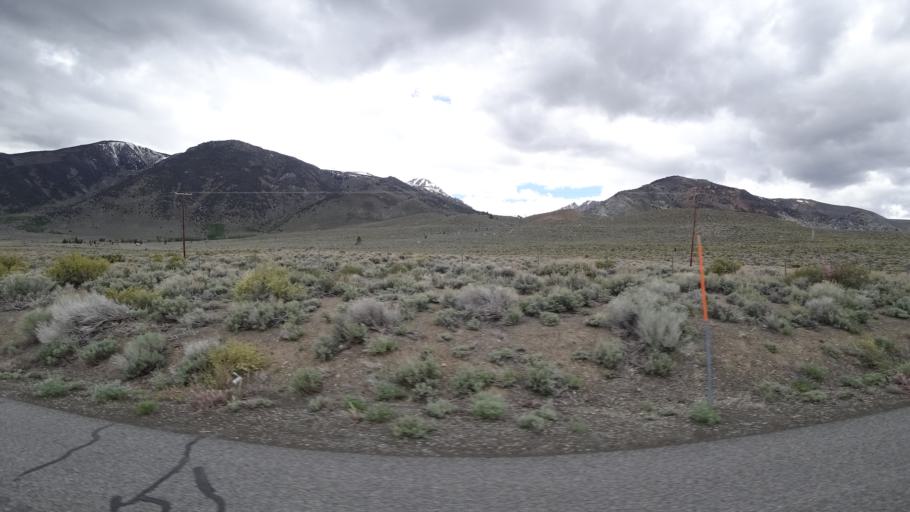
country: US
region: California
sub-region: Mono County
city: Bridgeport
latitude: 38.0319
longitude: -119.1567
